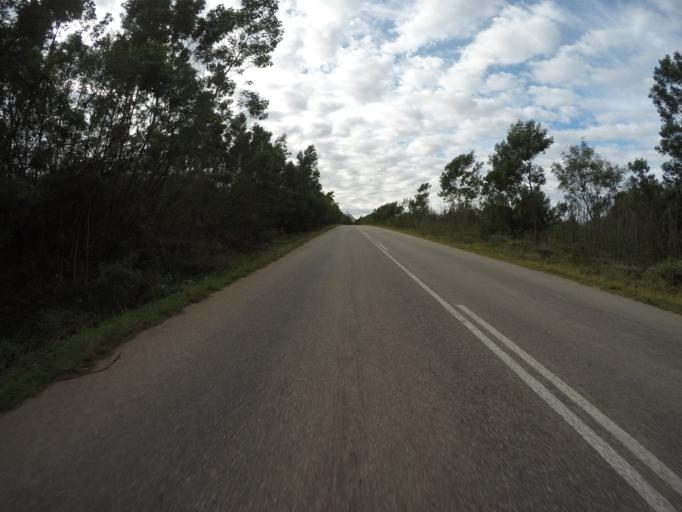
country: ZA
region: Eastern Cape
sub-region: Cacadu District Municipality
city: Kareedouw
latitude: -34.0170
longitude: 24.3414
